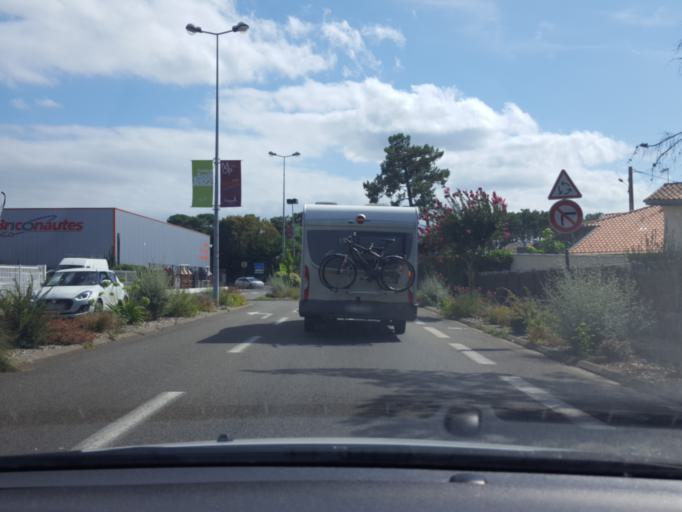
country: FR
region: Aquitaine
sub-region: Departement des Landes
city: Capbreton
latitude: 43.6399
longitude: -1.4257
